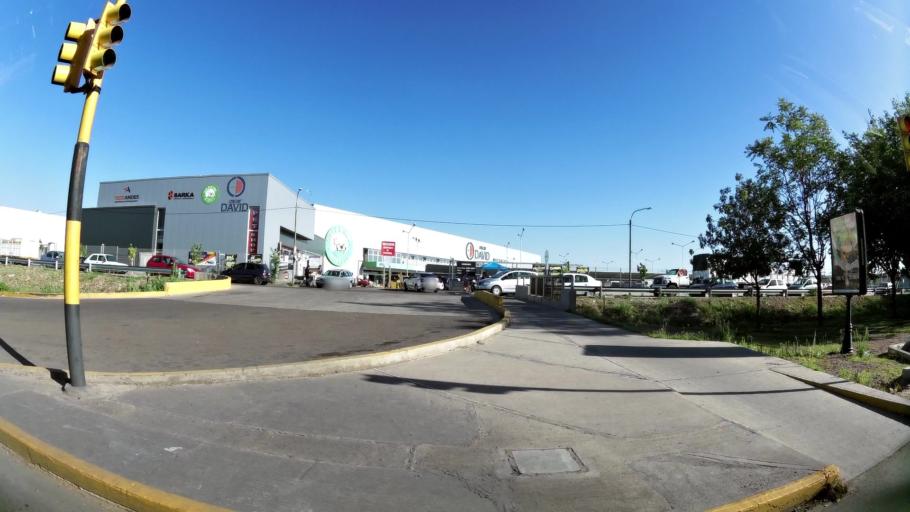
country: AR
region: Mendoza
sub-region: Departamento de Godoy Cruz
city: Godoy Cruz
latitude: -32.9271
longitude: -68.8346
